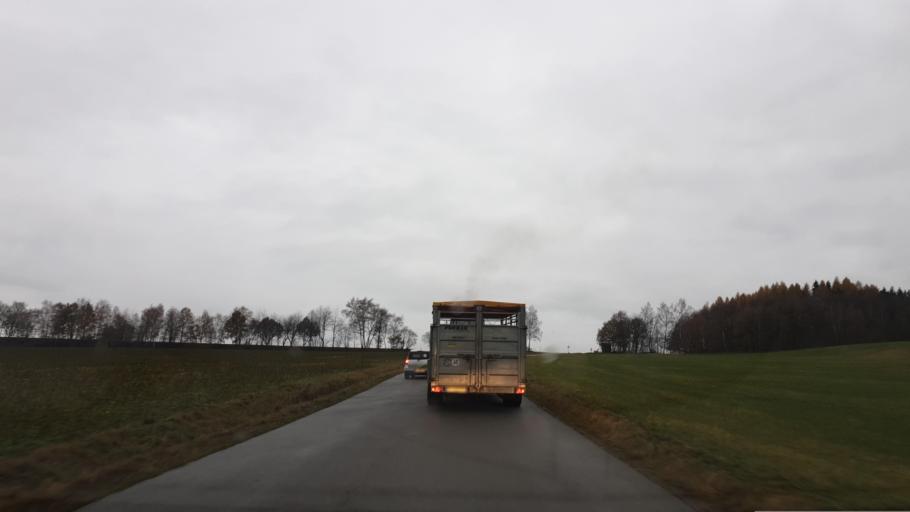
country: DE
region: Saxony
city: Zwonitz
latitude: 50.6499
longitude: 12.8054
